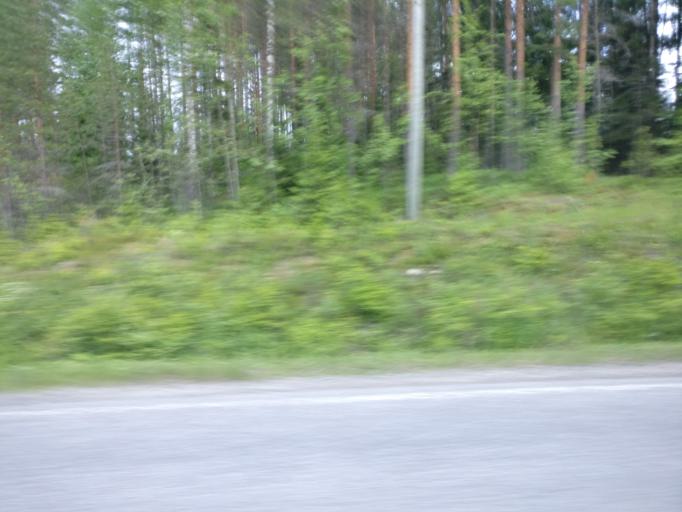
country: FI
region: Southern Savonia
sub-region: Savonlinna
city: Savonlinna
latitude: 61.9600
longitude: 28.9317
